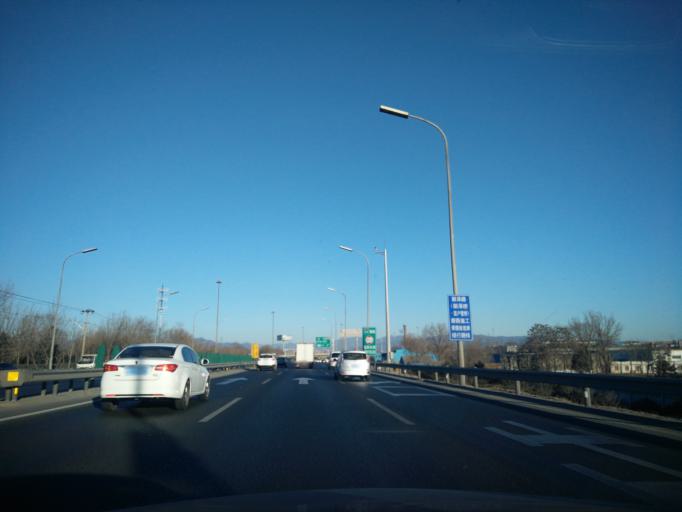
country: CN
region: Beijing
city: Fengtai
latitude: 39.8391
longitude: 116.2241
